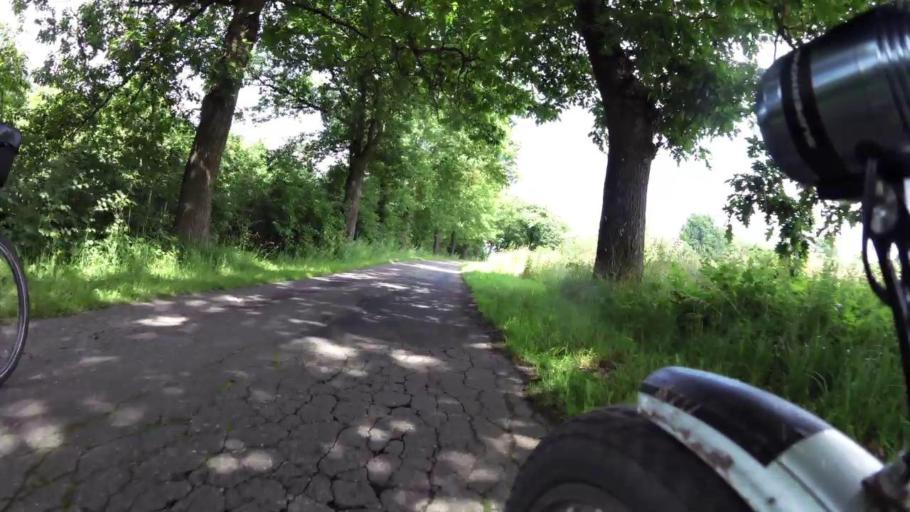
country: PL
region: West Pomeranian Voivodeship
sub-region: Powiat bialogardzki
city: Bialogard
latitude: 53.9419
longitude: 15.9833
